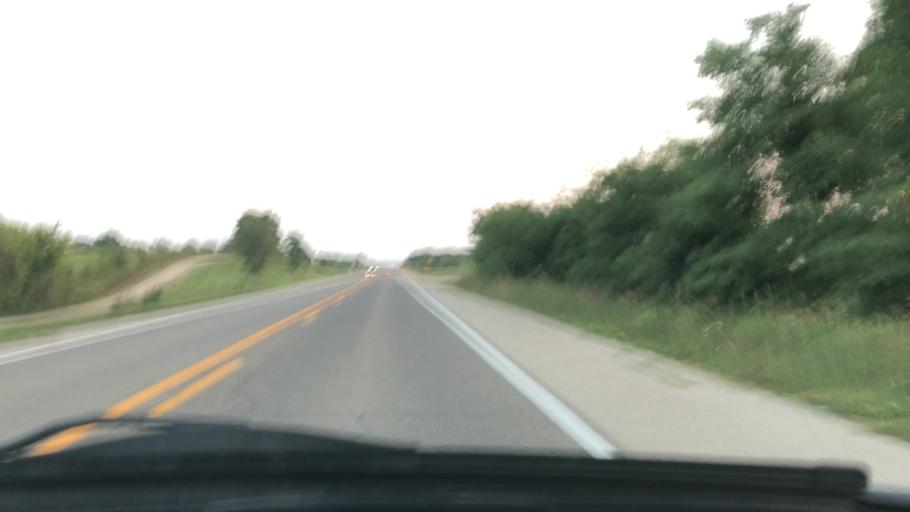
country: US
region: Iowa
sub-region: Henry County
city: Mount Pleasant
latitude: 40.9411
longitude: -91.5399
